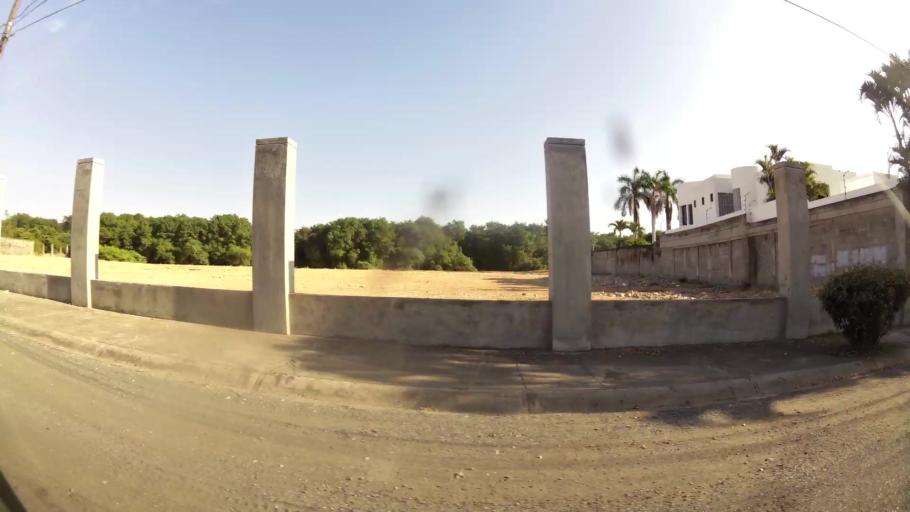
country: EC
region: Guayas
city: Santa Lucia
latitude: -2.1952
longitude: -79.9703
